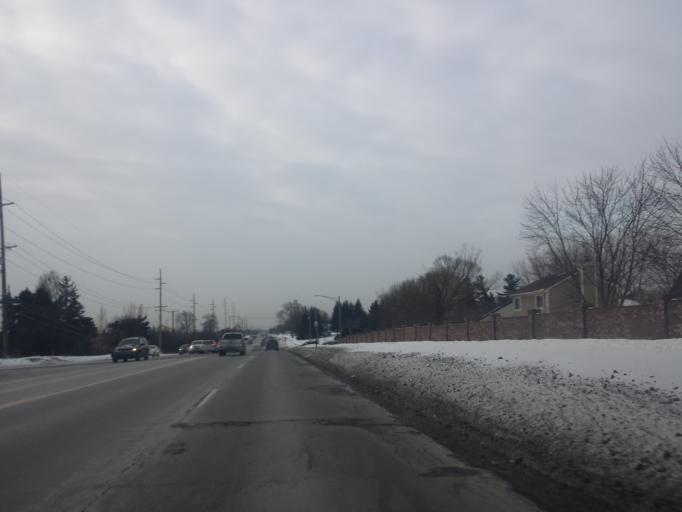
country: US
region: Michigan
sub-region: Oakland County
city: Rochester Hills
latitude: 42.6589
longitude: -83.1330
